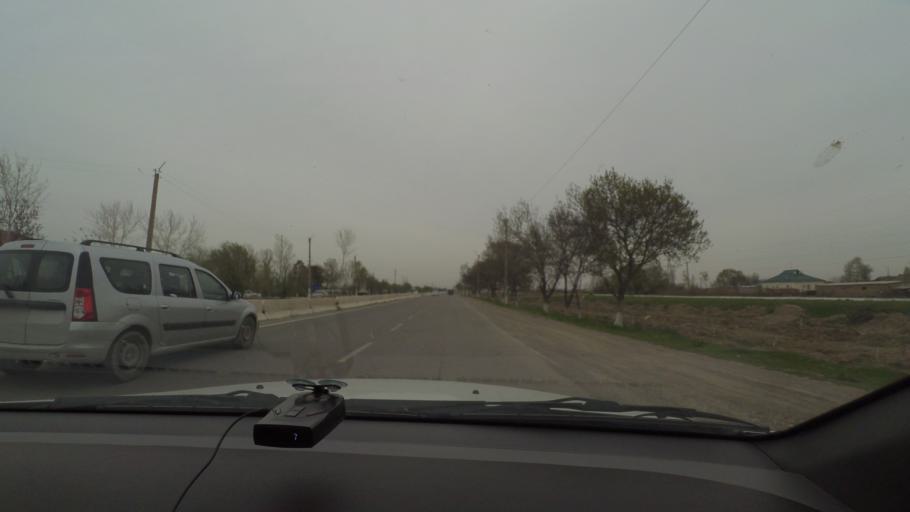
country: UZ
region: Sirdaryo
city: Guliston
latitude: 40.4891
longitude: 68.7393
